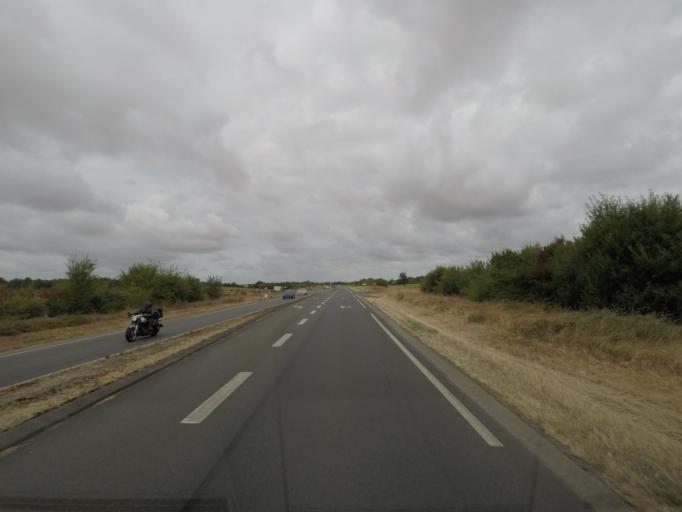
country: FR
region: Poitou-Charentes
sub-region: Departement des Deux-Sevres
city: Thorigne
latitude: 46.2838
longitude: -0.2623
